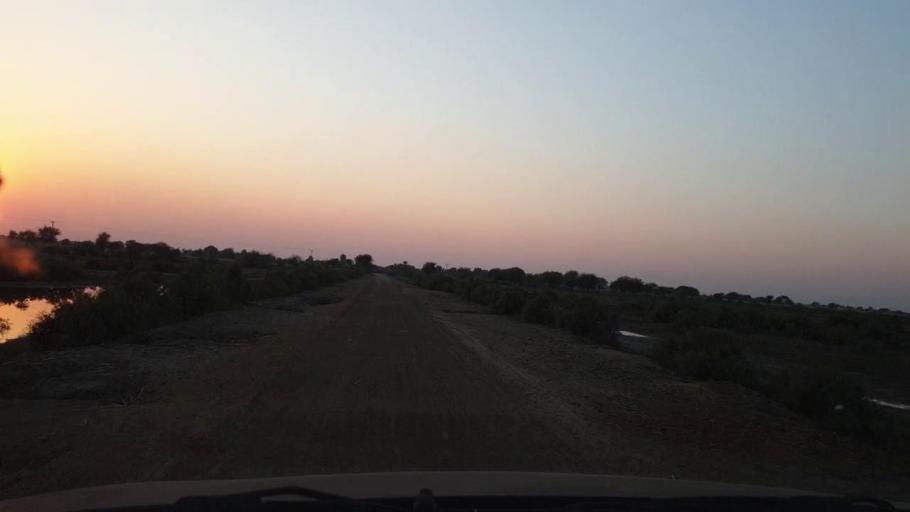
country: PK
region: Sindh
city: Jhol
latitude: 25.9367
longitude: 68.9641
